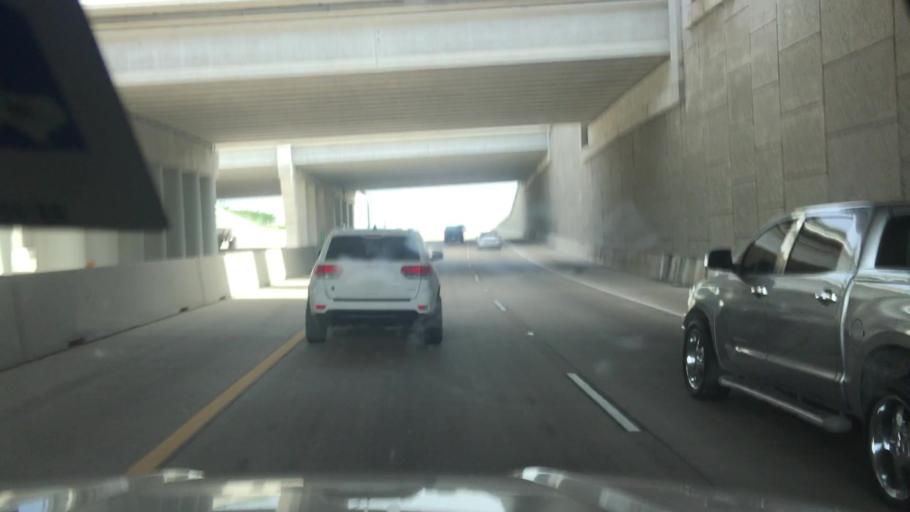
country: US
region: Texas
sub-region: Dallas County
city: Grand Prairie
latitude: 32.7417
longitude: -97.0203
